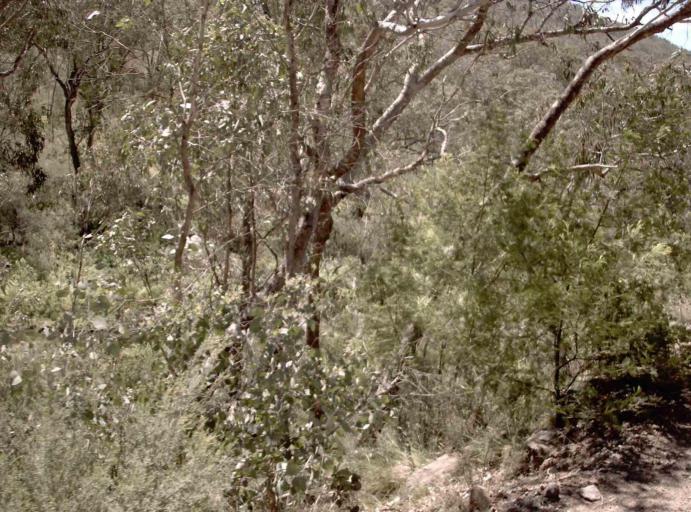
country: AU
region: New South Wales
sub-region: Snowy River
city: Jindabyne
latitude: -37.0764
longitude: 148.4924
